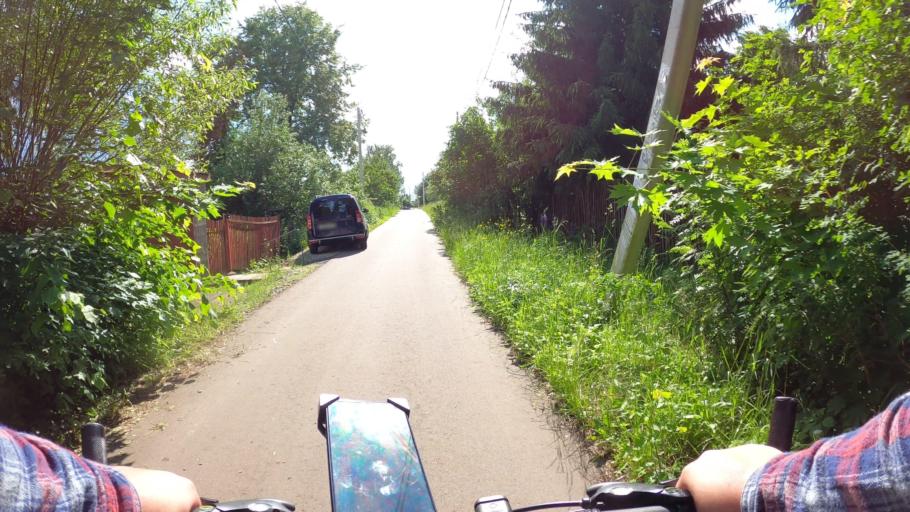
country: RU
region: Moskovskaya
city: Konobeyevo
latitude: 55.3911
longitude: 38.7013
